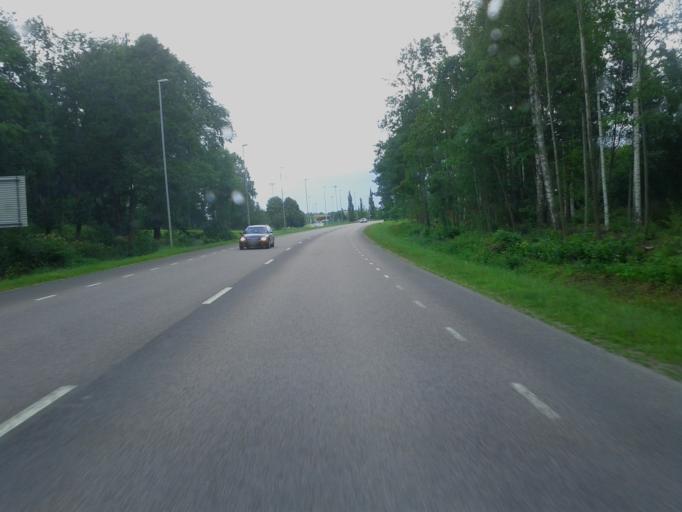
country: SE
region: Vaestmanland
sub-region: Sala Kommun
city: Sala
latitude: 59.9168
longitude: 16.5866
